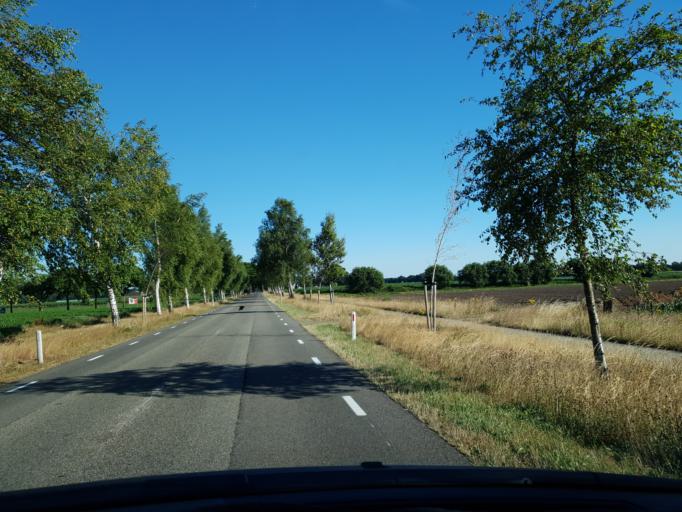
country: NL
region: North Brabant
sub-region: Gemeente Rucphen
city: Rucphen
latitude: 51.5091
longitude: 4.5808
